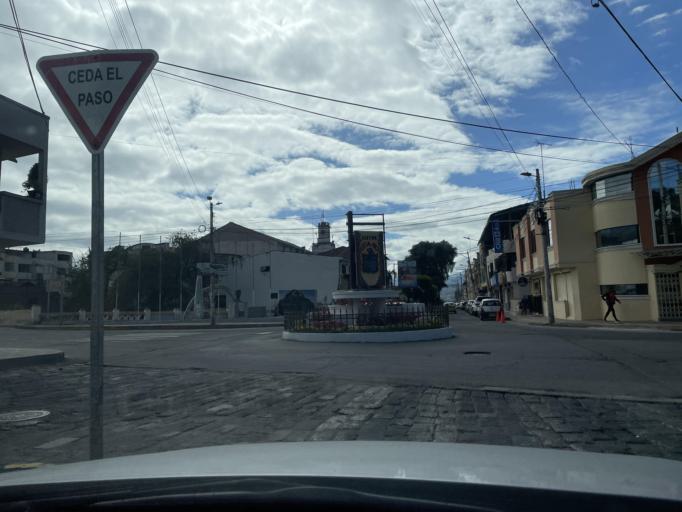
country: EC
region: Chimborazo
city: Guano
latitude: -1.6080
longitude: -78.6464
